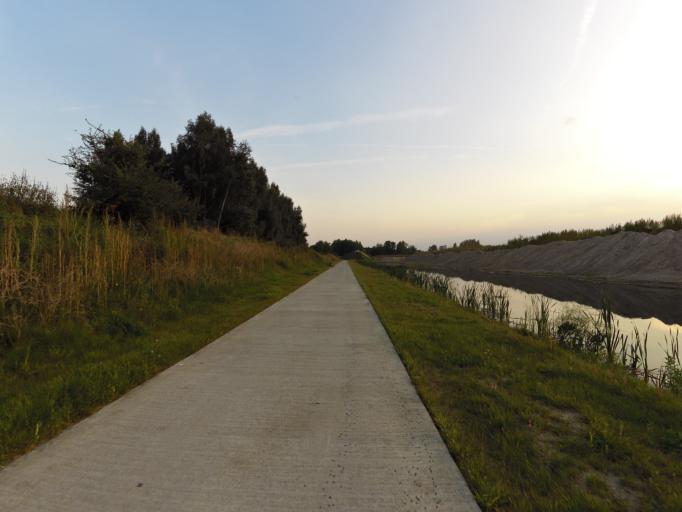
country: DE
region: North Rhine-Westphalia
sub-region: Regierungsbezirk Dusseldorf
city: Kleve
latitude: 51.8668
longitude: 6.1405
